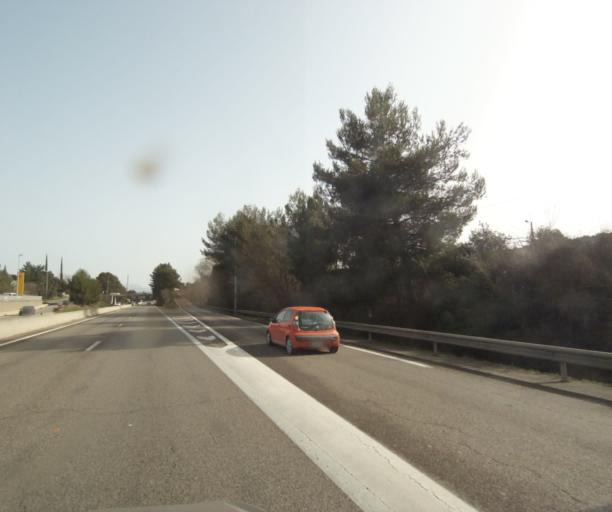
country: FR
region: Provence-Alpes-Cote d'Azur
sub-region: Departement des Bouches-du-Rhone
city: Simiane-Collongue
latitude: 43.4484
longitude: 5.4464
